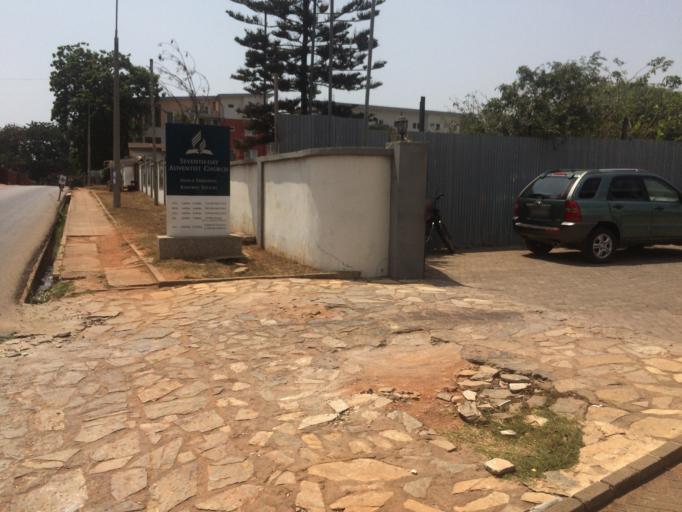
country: GH
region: Greater Accra
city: Accra
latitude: 5.5688
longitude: -0.1887
